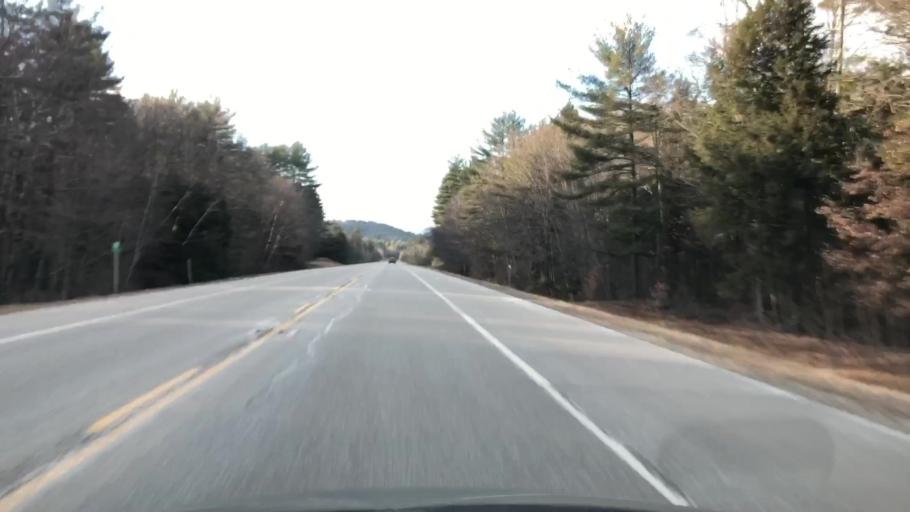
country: US
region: New Hampshire
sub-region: Hillsborough County
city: Milford
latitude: 42.8323
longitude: -71.6852
